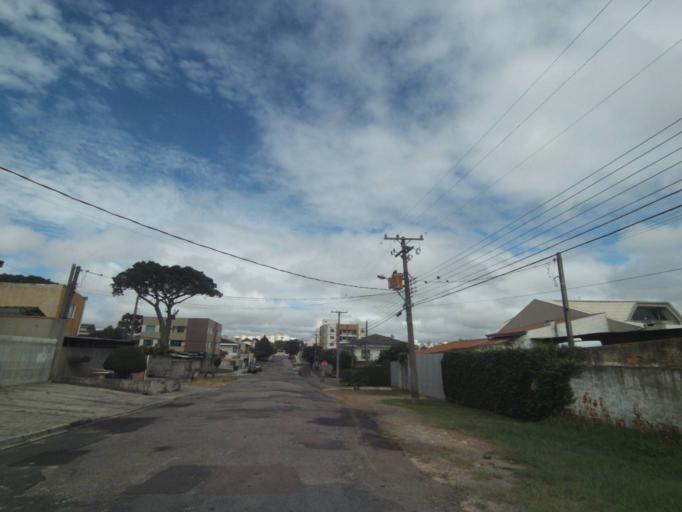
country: BR
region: Parana
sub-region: Curitiba
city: Curitiba
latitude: -25.4819
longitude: -49.2817
